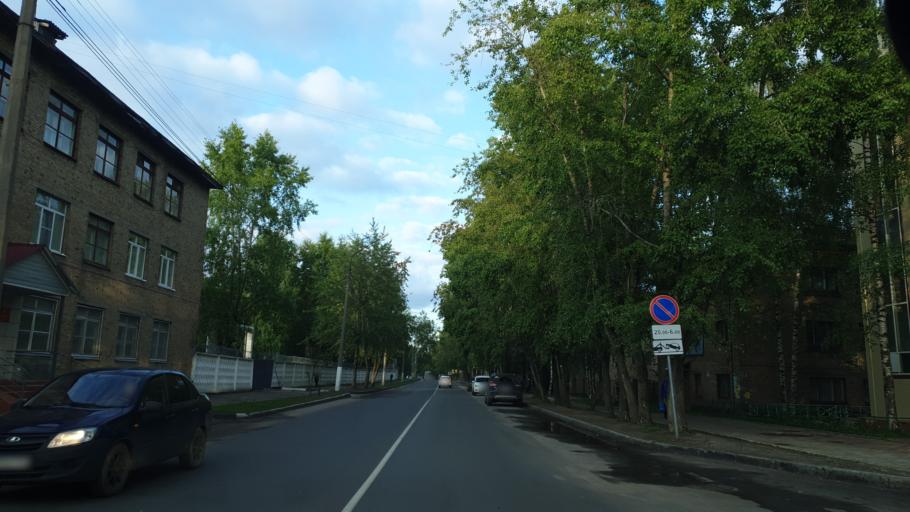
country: RU
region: Komi Republic
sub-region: Syktyvdinskiy Rayon
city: Syktyvkar
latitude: 61.6645
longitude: 50.7922
